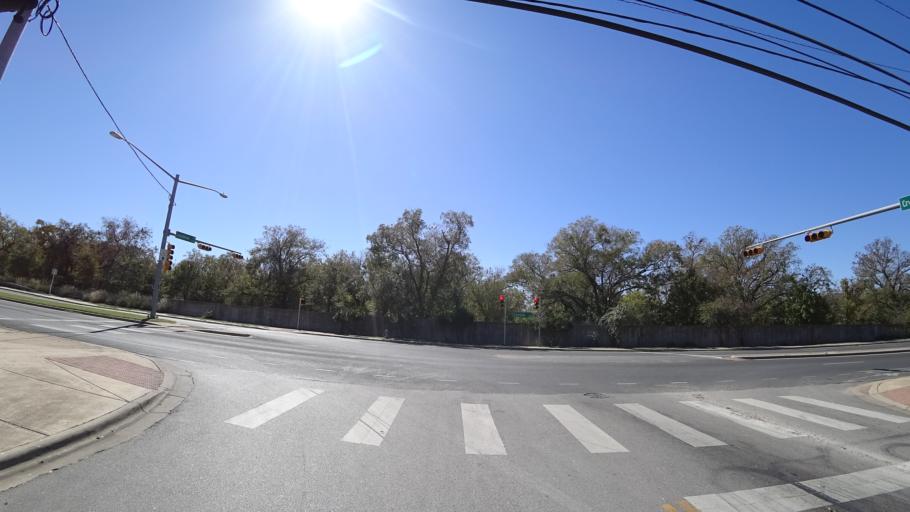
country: US
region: Texas
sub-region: Travis County
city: Hornsby Bend
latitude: 30.3031
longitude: -97.6538
